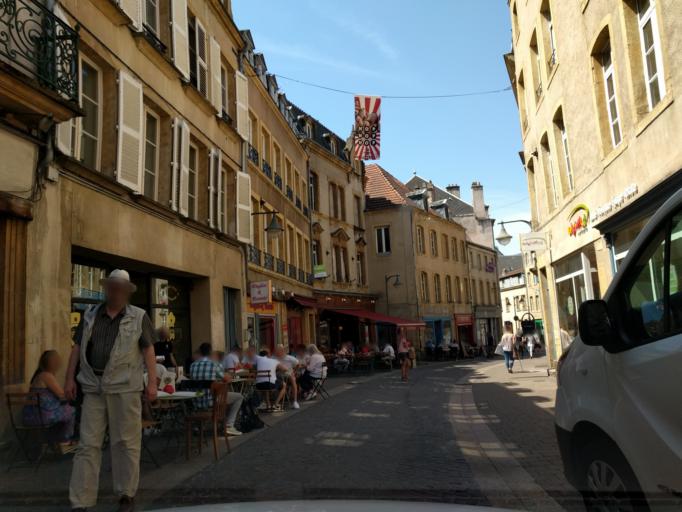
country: FR
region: Lorraine
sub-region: Departement de la Moselle
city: Metz
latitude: 49.1191
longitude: 6.1721
